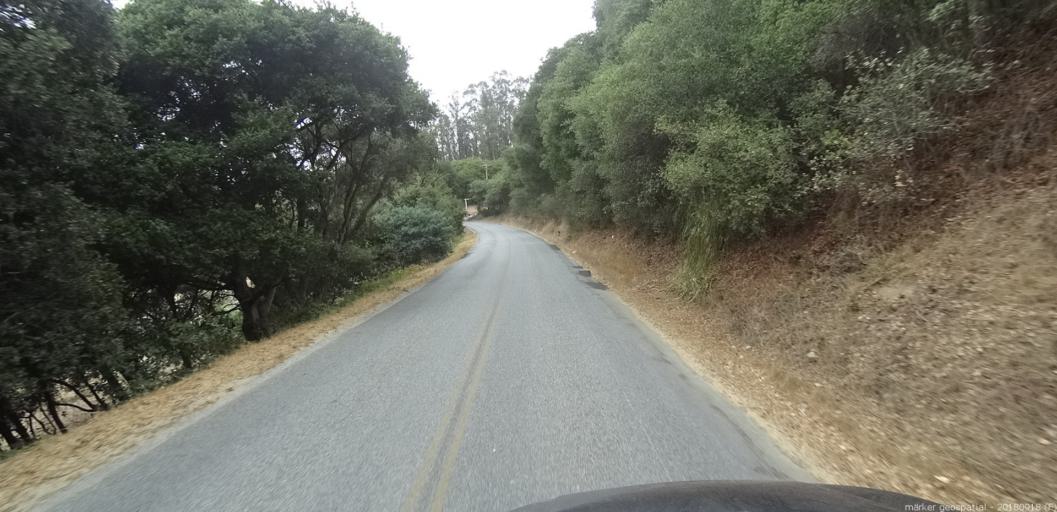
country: US
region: California
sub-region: Monterey County
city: Prunedale
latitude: 36.7748
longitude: -121.6603
